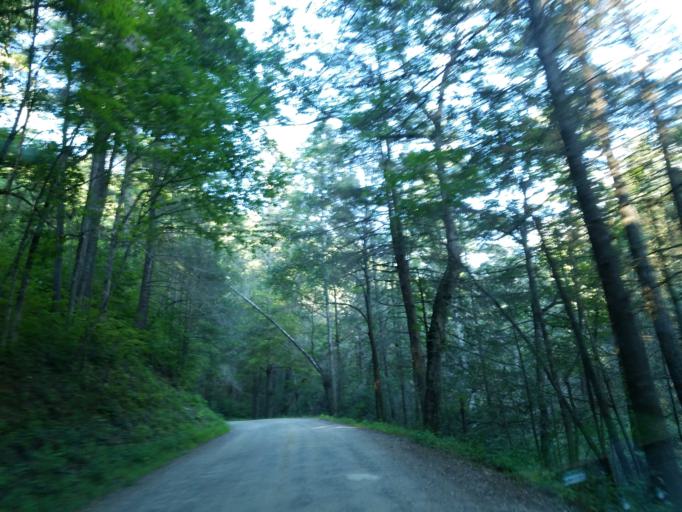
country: US
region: Georgia
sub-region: Union County
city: Blairsville
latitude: 34.7622
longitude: -84.0788
